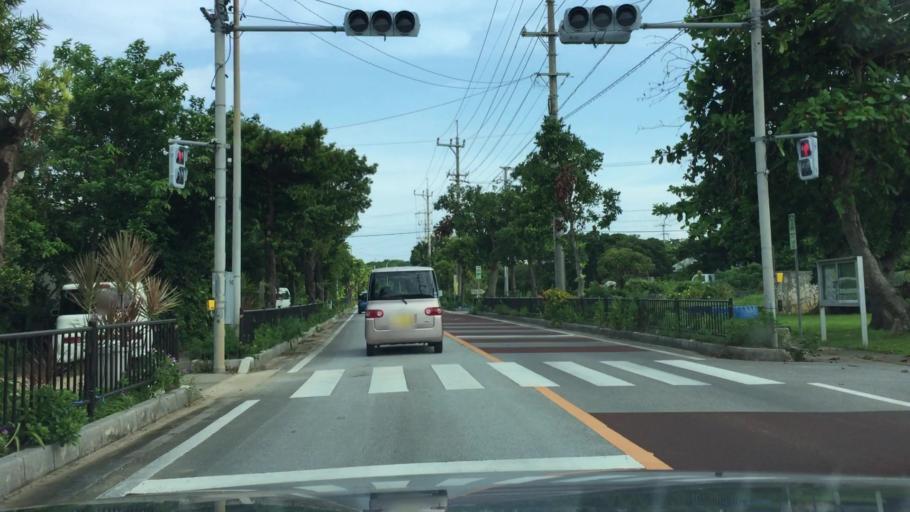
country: JP
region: Okinawa
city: Ishigaki
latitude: 24.4537
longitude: 124.2488
